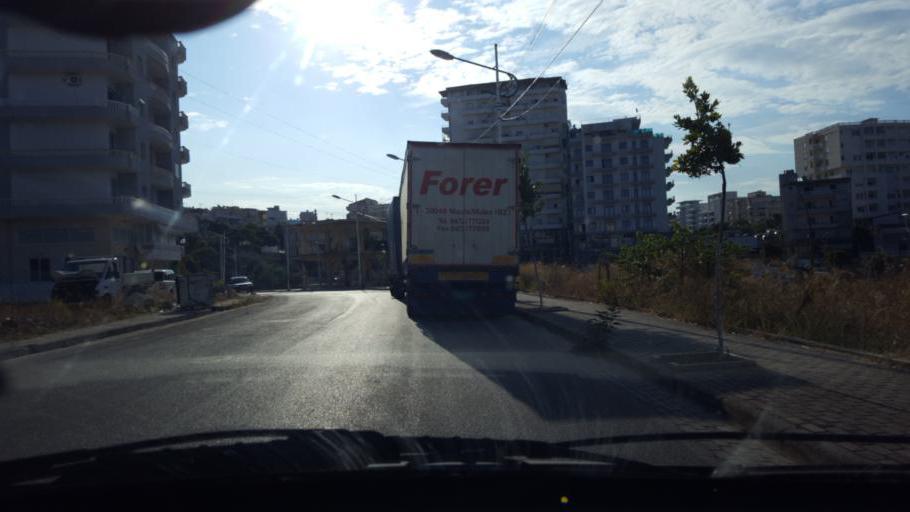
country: AL
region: Vlore
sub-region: Rrethi i Sarandes
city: Sarande
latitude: 39.8746
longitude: 19.9896
